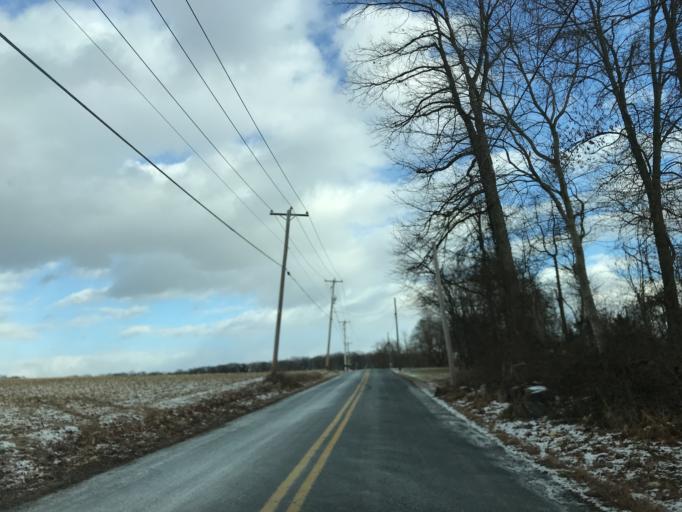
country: US
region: Pennsylvania
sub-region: York County
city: Susquehanna Trails
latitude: 39.6626
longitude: -76.3883
